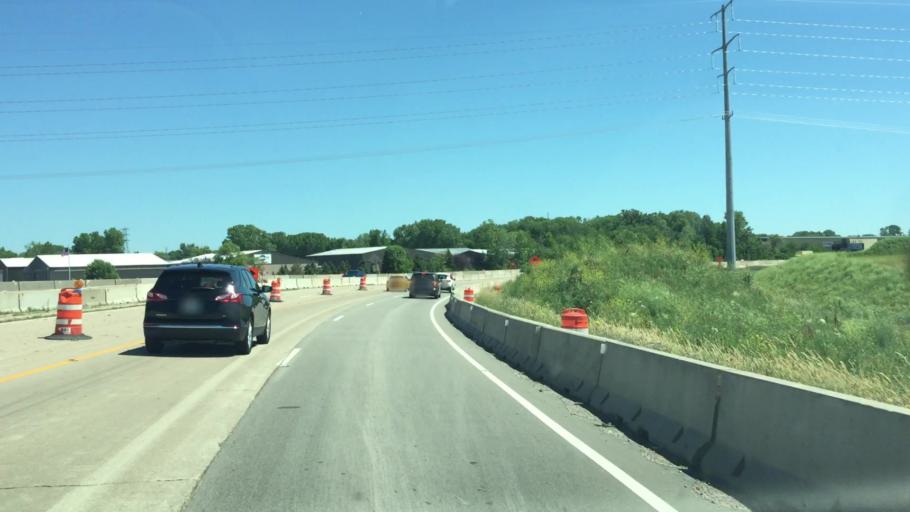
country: US
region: Wisconsin
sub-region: Winnebago County
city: Menasha
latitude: 44.2323
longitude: -88.4402
